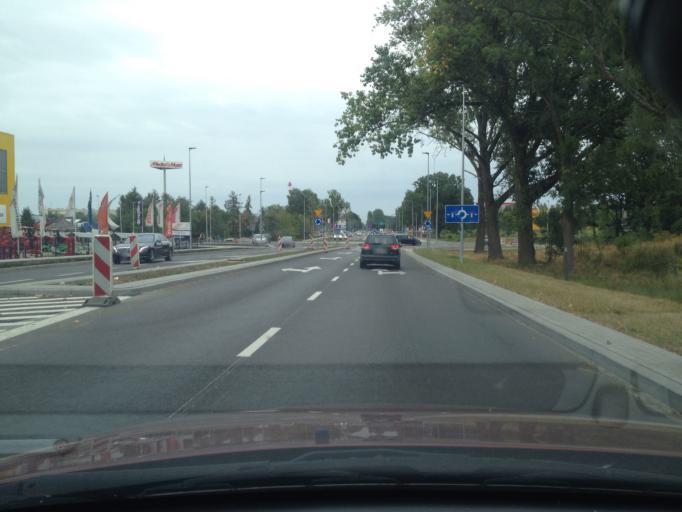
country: PL
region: Lubusz
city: Gorzow Wielkopolski
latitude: 52.7391
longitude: 15.1927
